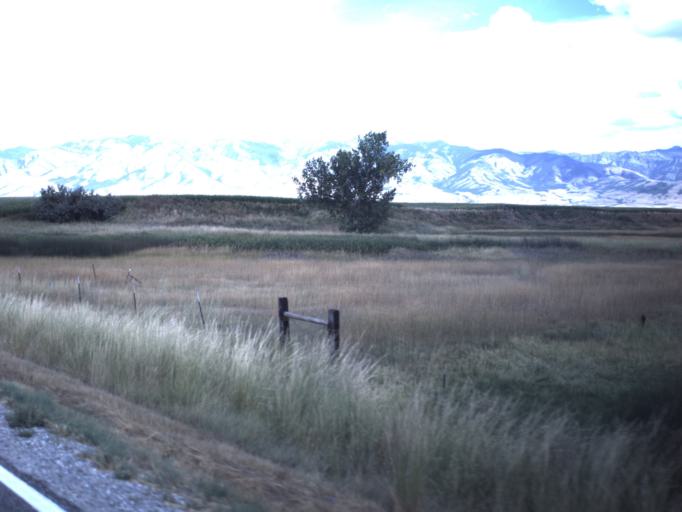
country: US
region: Utah
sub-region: Cache County
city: Lewiston
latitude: 41.9233
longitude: -111.9044
